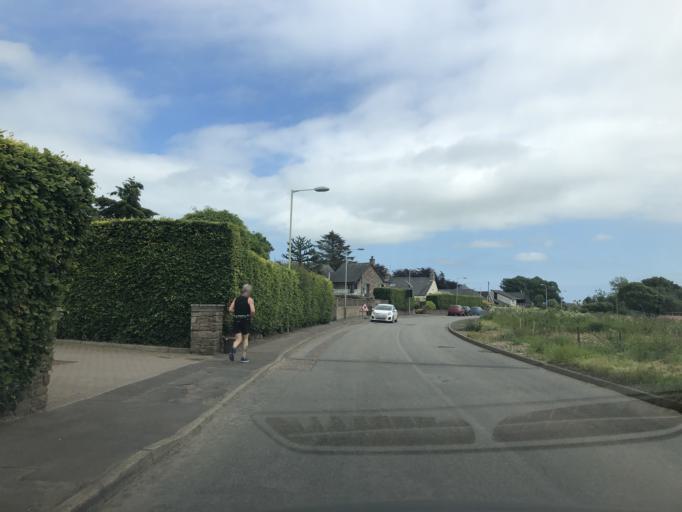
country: GB
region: Scotland
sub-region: Angus
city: Brechin
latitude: 56.7367
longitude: -2.6774
